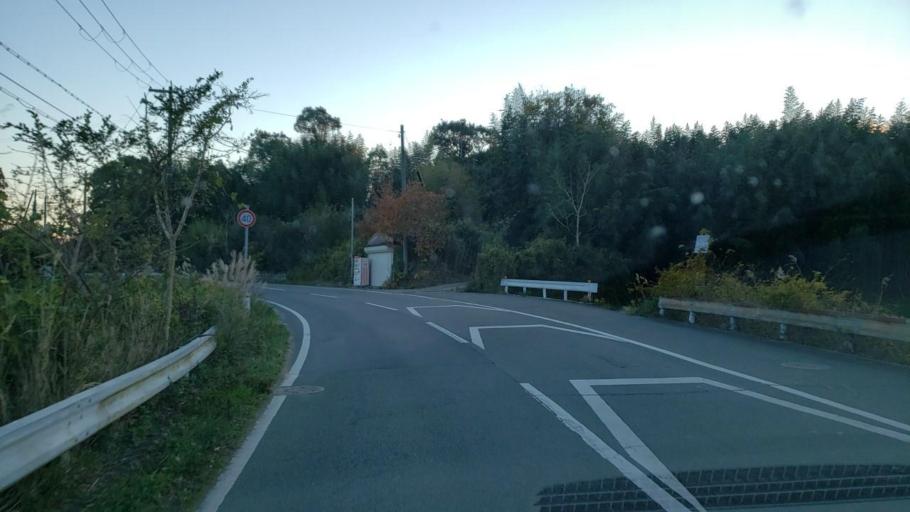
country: JP
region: Hyogo
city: Fukura
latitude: 34.3461
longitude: 134.7826
